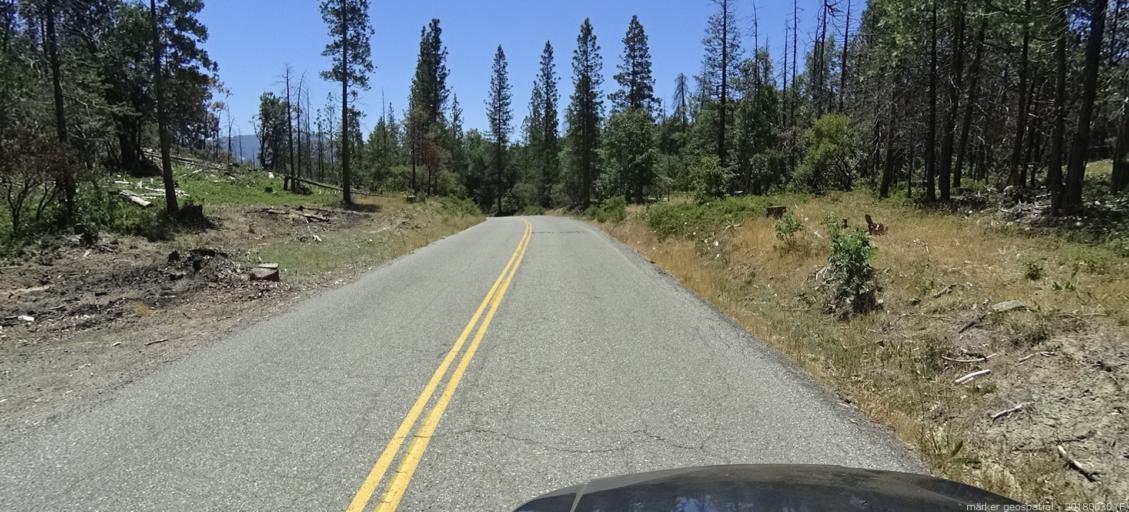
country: US
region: California
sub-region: Fresno County
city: Auberry
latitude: 37.2392
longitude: -119.3655
